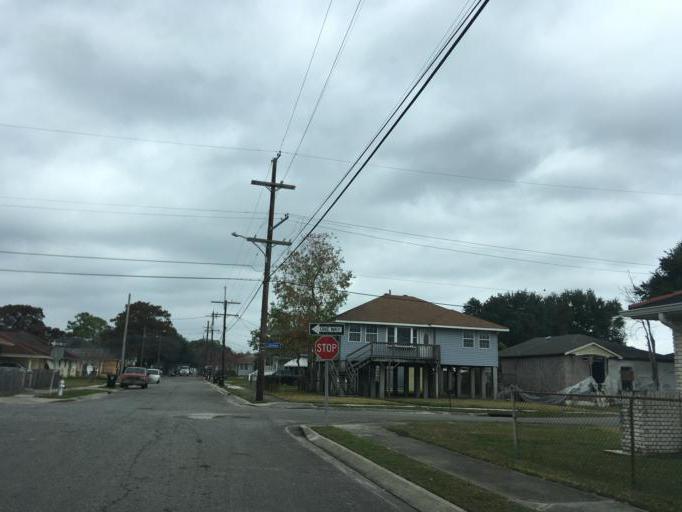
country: US
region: Louisiana
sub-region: Orleans Parish
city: New Orleans
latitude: 29.9938
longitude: -90.0575
